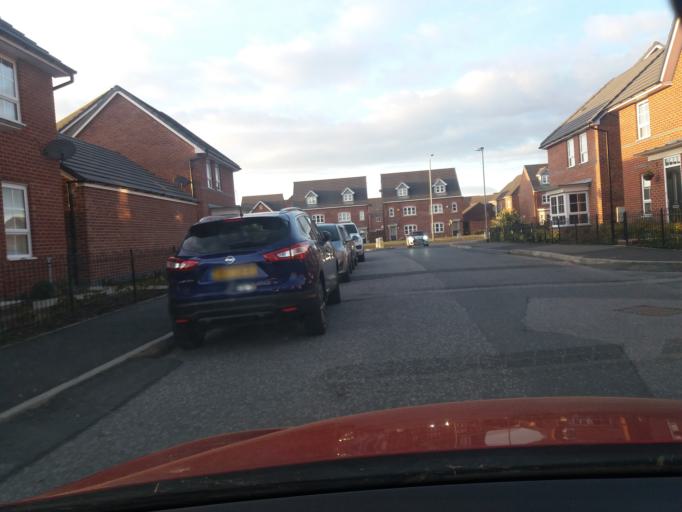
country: GB
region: England
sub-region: Lancashire
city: Euxton
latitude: 53.6763
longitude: -2.6606
